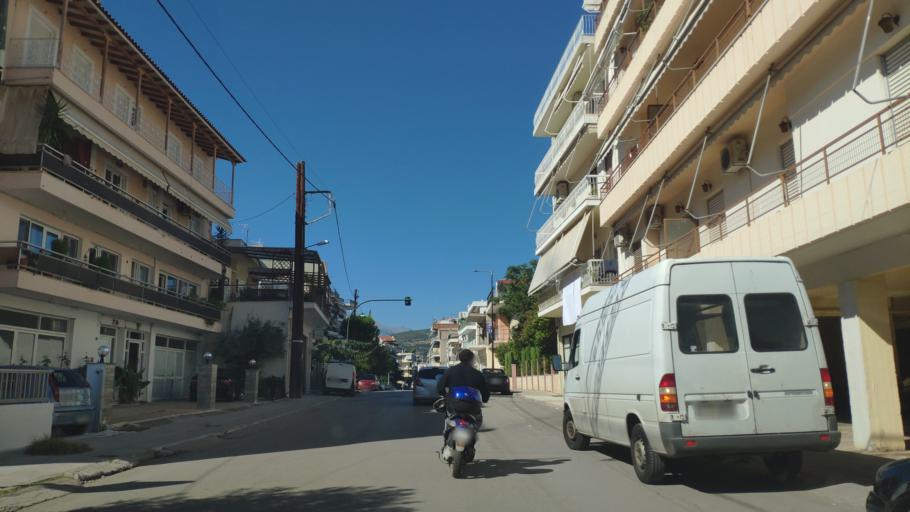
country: GR
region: Central Greece
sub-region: Nomos Voiotias
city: Livadeia
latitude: 38.4406
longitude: 22.8681
